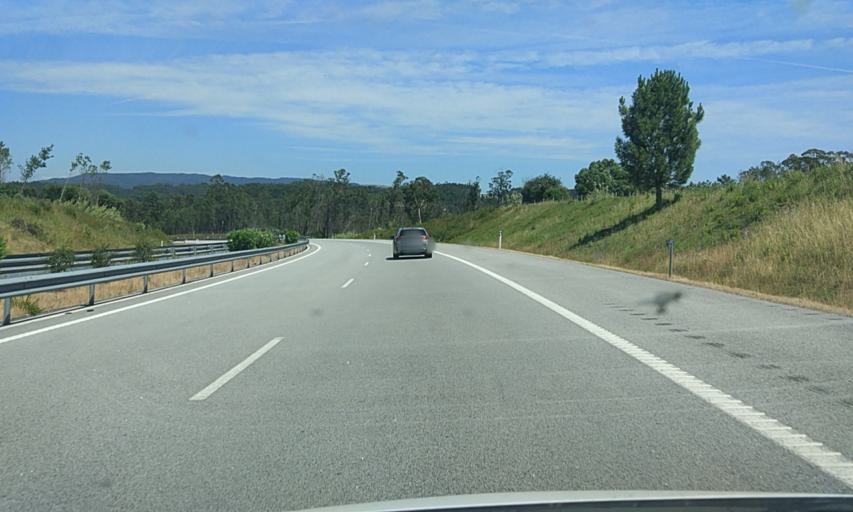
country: PT
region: Aveiro
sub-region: Mealhada
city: Pampilhosa do Botao
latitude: 40.2719
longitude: -8.5003
